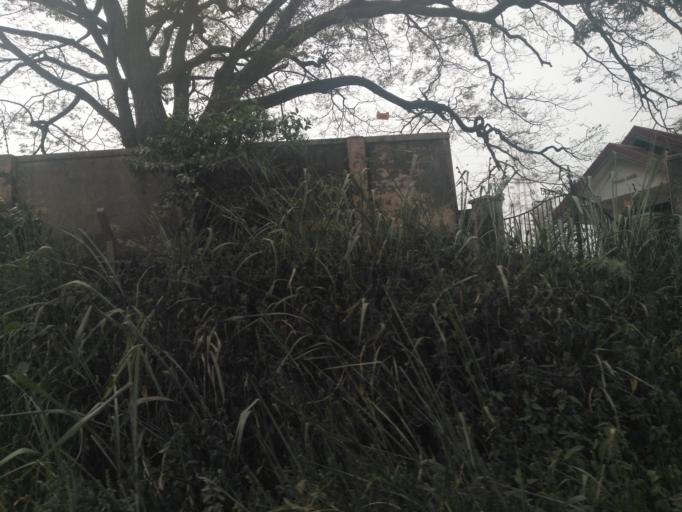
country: GH
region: Ashanti
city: Kumasi
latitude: 6.6785
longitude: -1.6173
